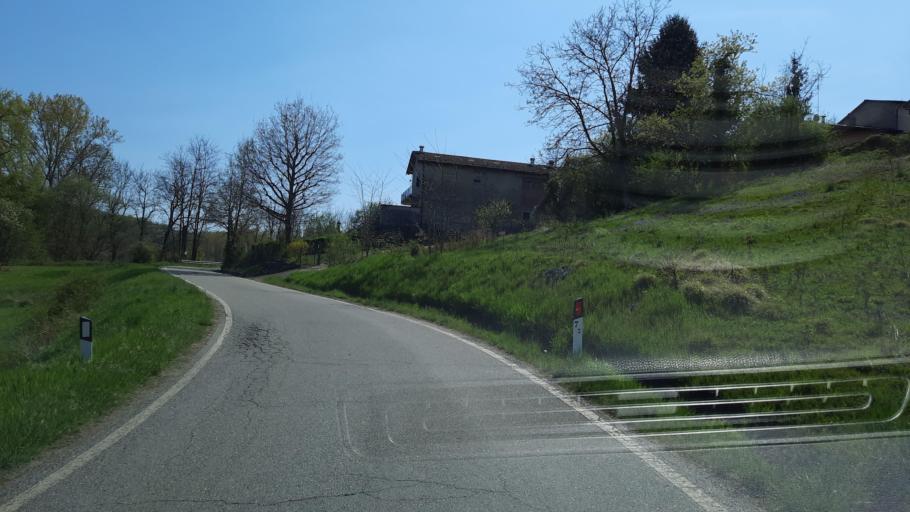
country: IT
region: Piedmont
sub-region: Provincia di Alessandria
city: Moncestino
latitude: 45.1514
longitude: 8.1285
